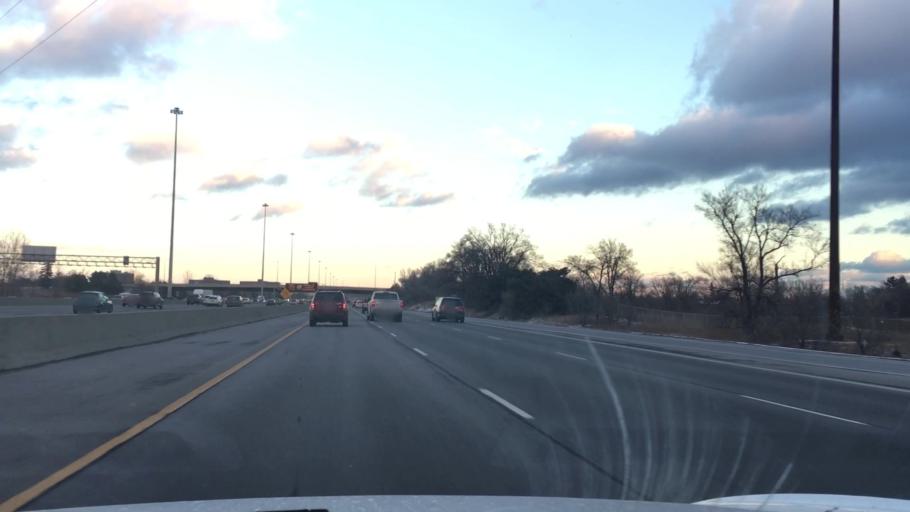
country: CA
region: Ontario
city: Scarborough
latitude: 43.7966
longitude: -79.1921
